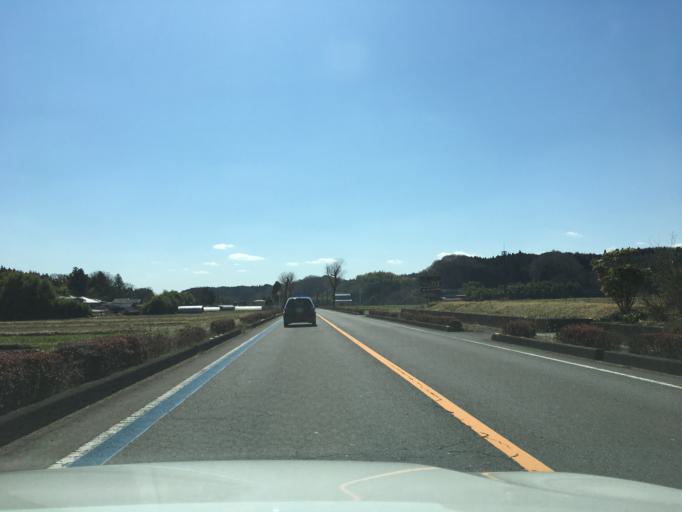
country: JP
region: Tochigi
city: Kuroiso
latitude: 36.9895
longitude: 140.1613
